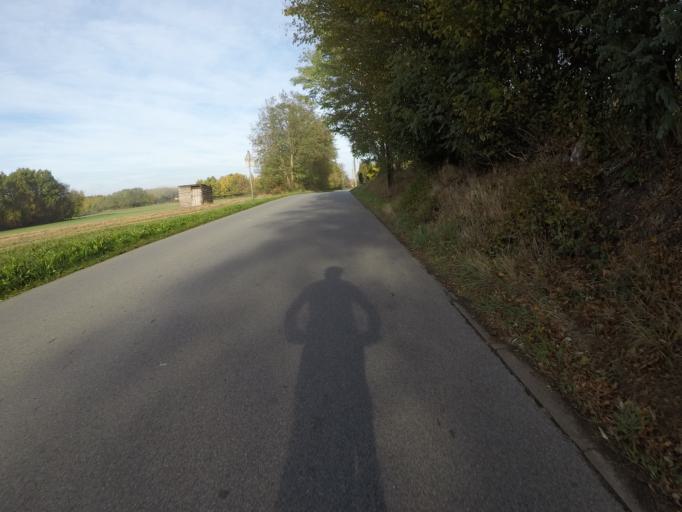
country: BE
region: Flanders
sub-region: Provincie Vlaams-Brabant
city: Begijnendijk
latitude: 50.9951
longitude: 4.7836
